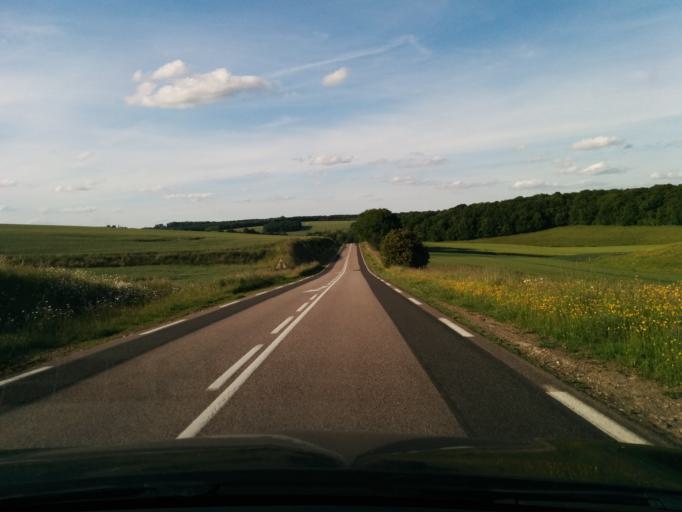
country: FR
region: Haute-Normandie
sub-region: Departement de l'Eure
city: Charleval
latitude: 49.3394
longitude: 1.4507
